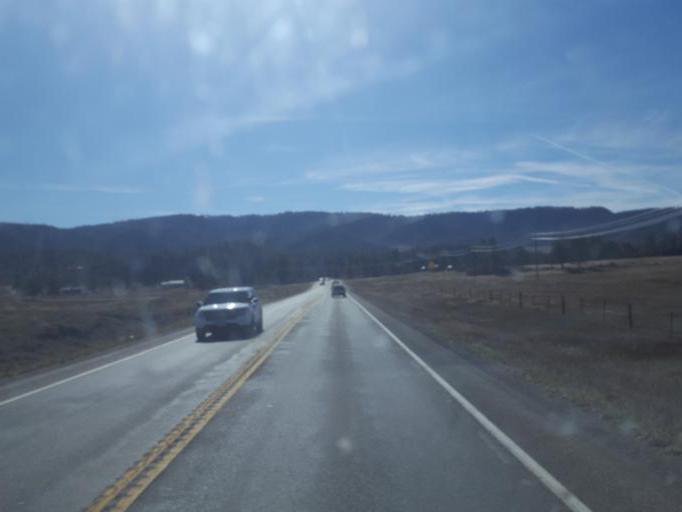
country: US
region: Colorado
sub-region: Archuleta County
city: Pagosa Springs
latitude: 37.2348
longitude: -107.1045
